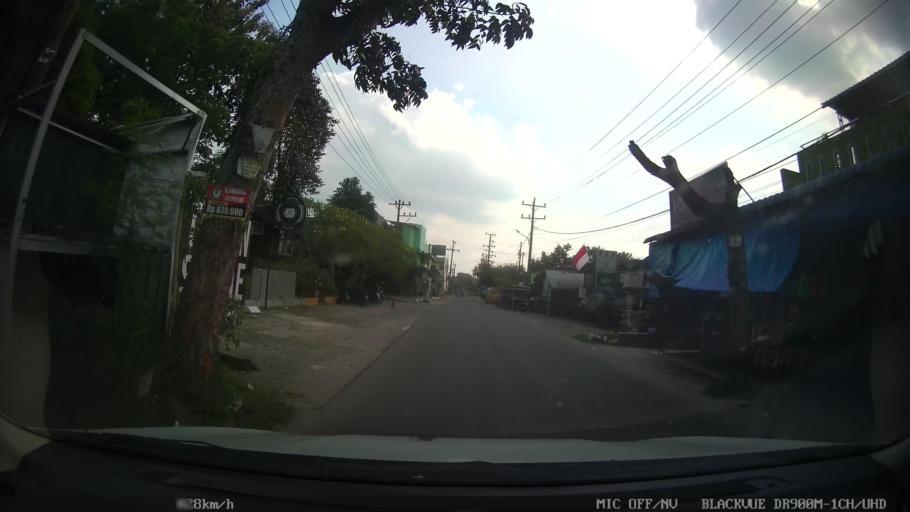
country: ID
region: North Sumatra
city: Binjai
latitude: 3.6361
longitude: 98.4904
